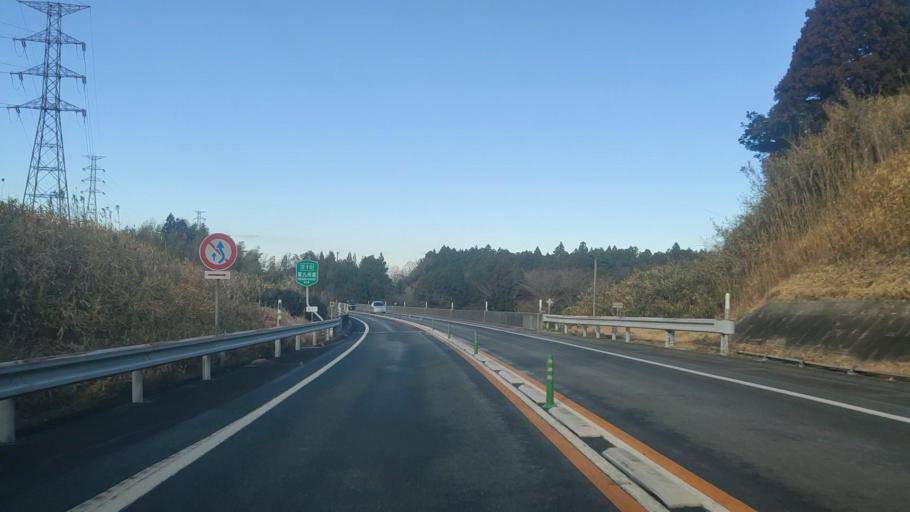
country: JP
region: Oita
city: Hiji
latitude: 33.3810
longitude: 131.4478
